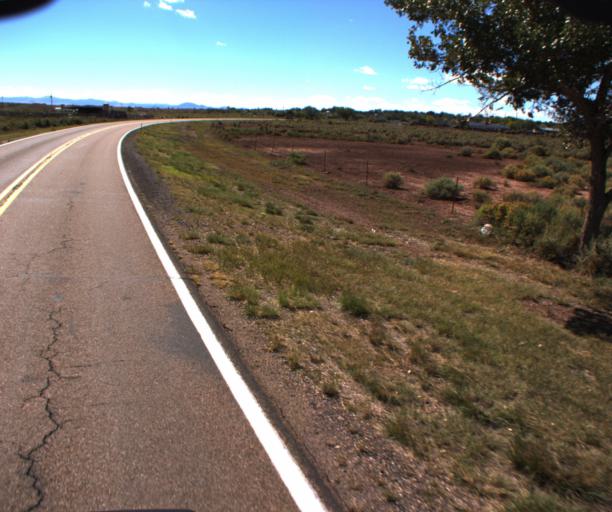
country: US
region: Arizona
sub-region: Apache County
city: Saint Johns
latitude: 34.5093
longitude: -109.3488
